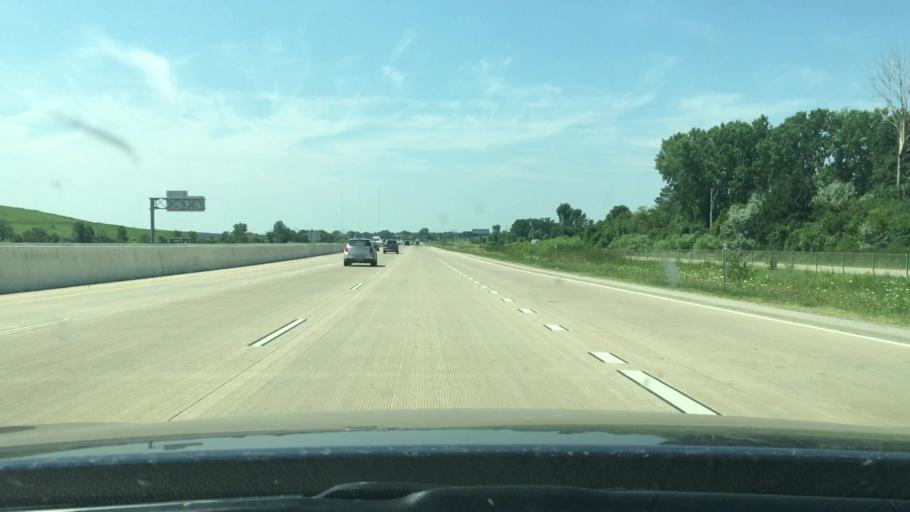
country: US
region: Wisconsin
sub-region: Winnebago County
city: Oshkosh
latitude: 44.0940
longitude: -88.5477
